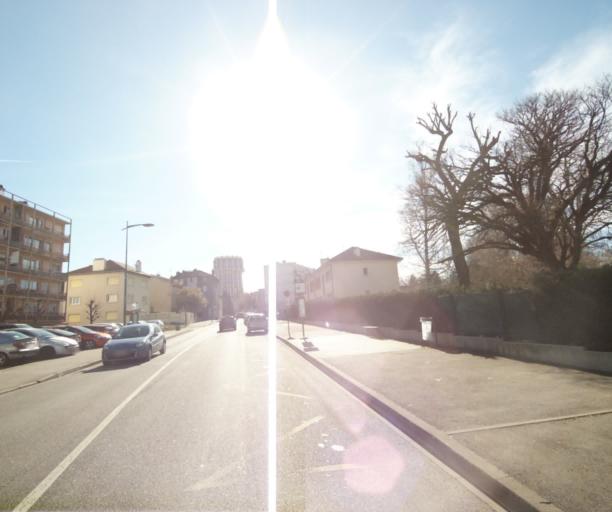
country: FR
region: Lorraine
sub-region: Departement de Meurthe-et-Moselle
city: Nancy
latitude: 48.6702
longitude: 6.1787
